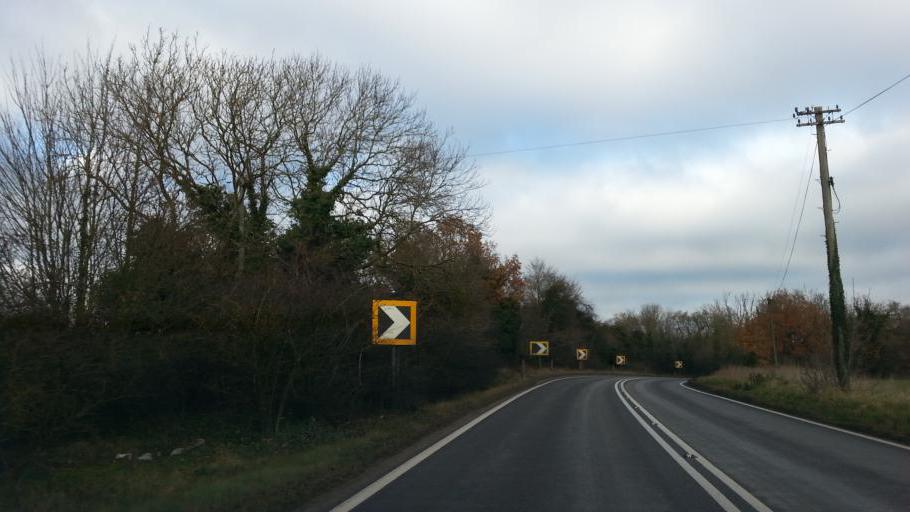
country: GB
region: England
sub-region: Suffolk
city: Ixworth
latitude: 52.3150
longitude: 0.8655
